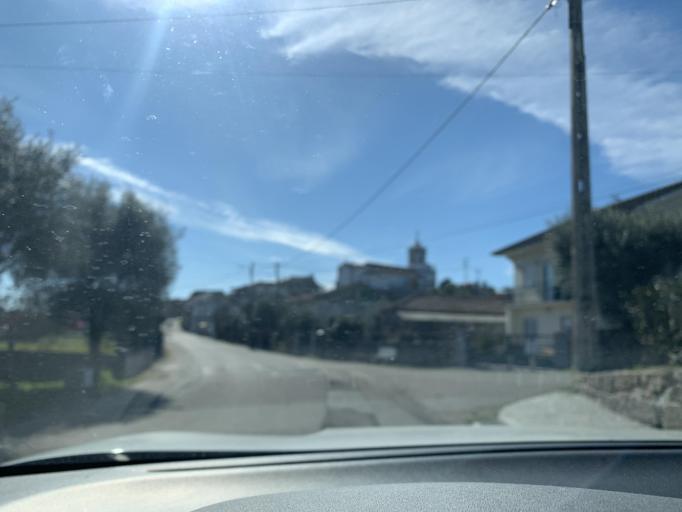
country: PT
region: Viseu
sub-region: Concelho de Tondela
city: Tondela
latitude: 40.5902
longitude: -8.0262
